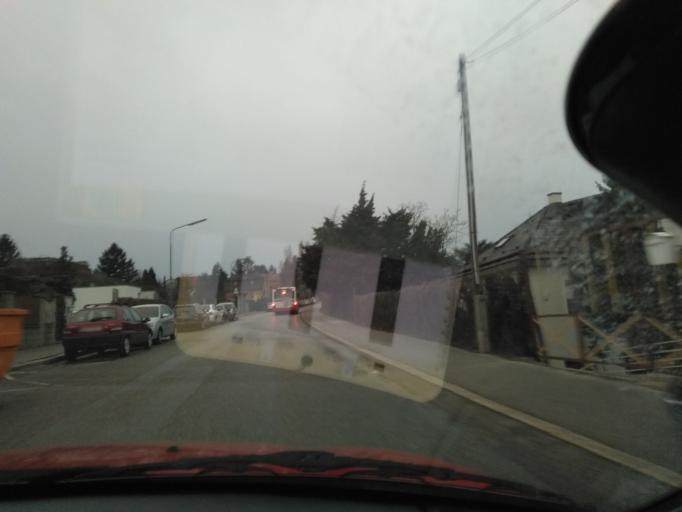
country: AT
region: Vienna
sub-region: Wien Stadt
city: Vienna
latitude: 48.2315
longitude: 16.3091
